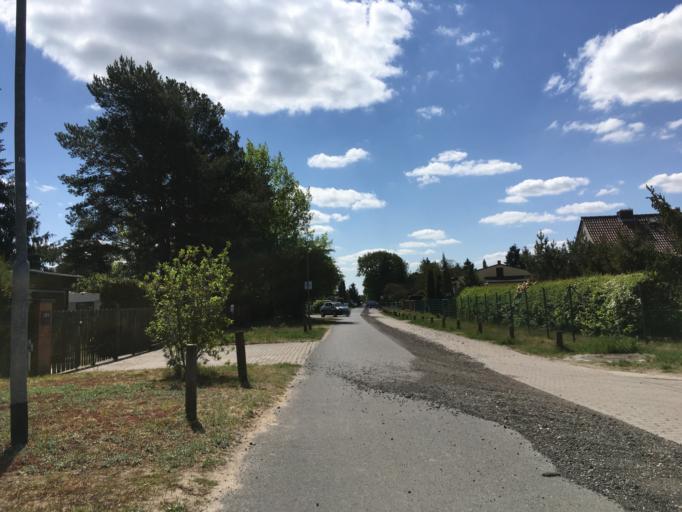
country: DE
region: Berlin
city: Blankenfelde
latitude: 52.6762
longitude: 13.3705
